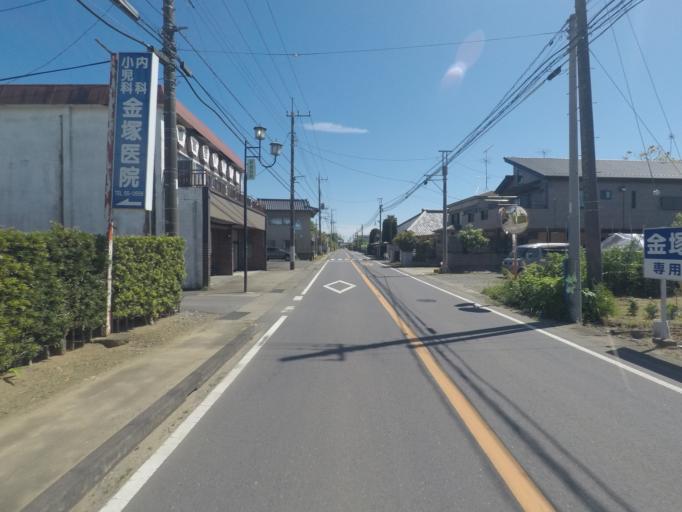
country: JP
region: Ibaraki
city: Inashiki
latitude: 36.0898
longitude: 140.4249
